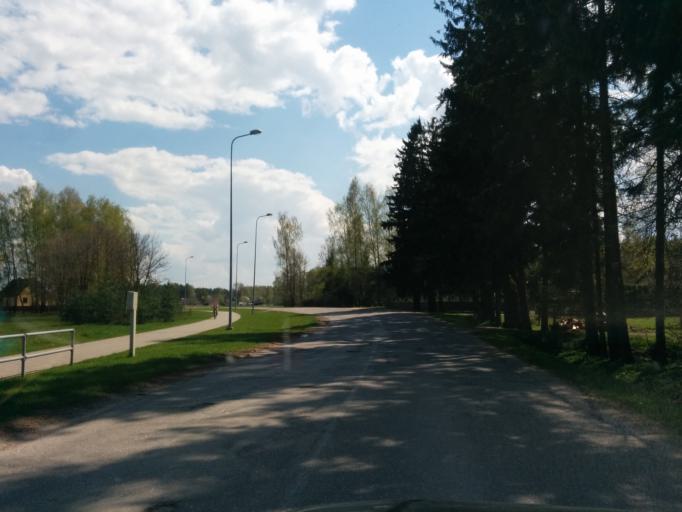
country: LV
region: Jelgava
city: Jelgava
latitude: 56.6194
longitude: 23.7722
